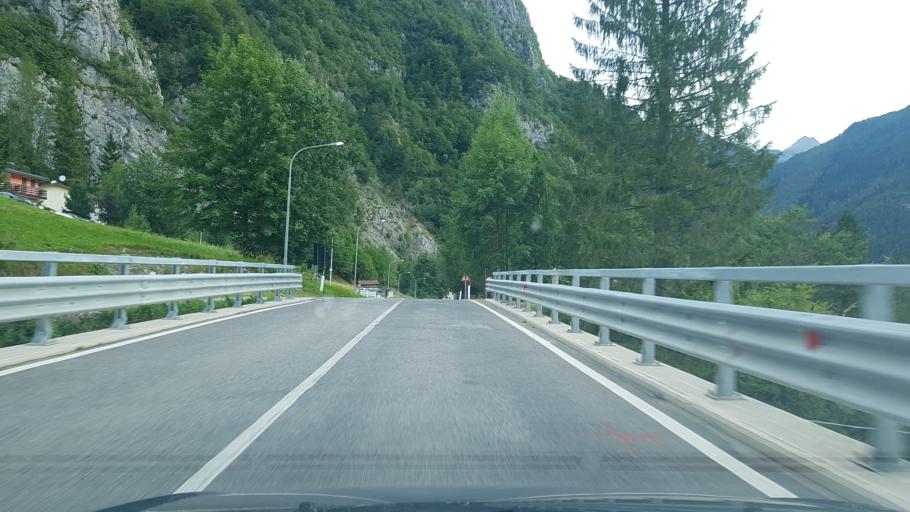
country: IT
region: Friuli Venezia Giulia
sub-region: Provincia di Udine
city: Forni Avoltri
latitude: 46.5830
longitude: 12.7646
